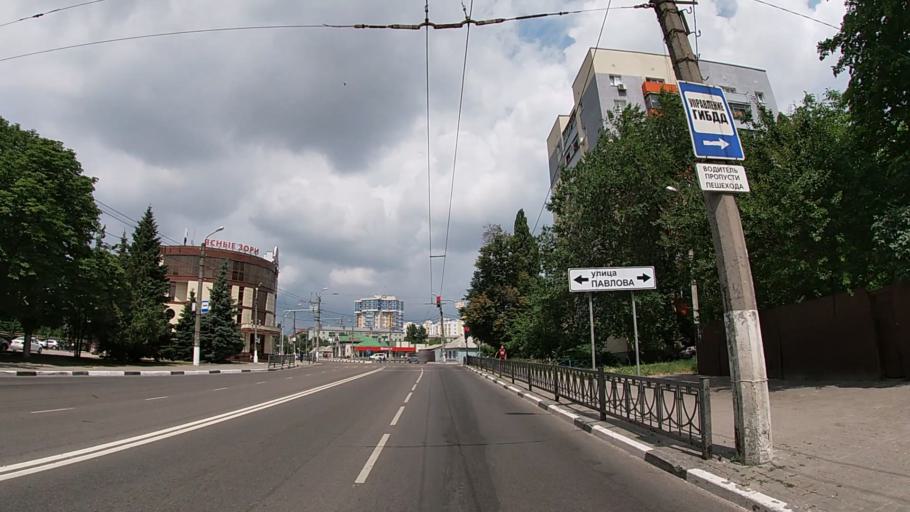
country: RU
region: Belgorod
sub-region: Belgorodskiy Rayon
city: Belgorod
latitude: 50.6088
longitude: 36.5919
